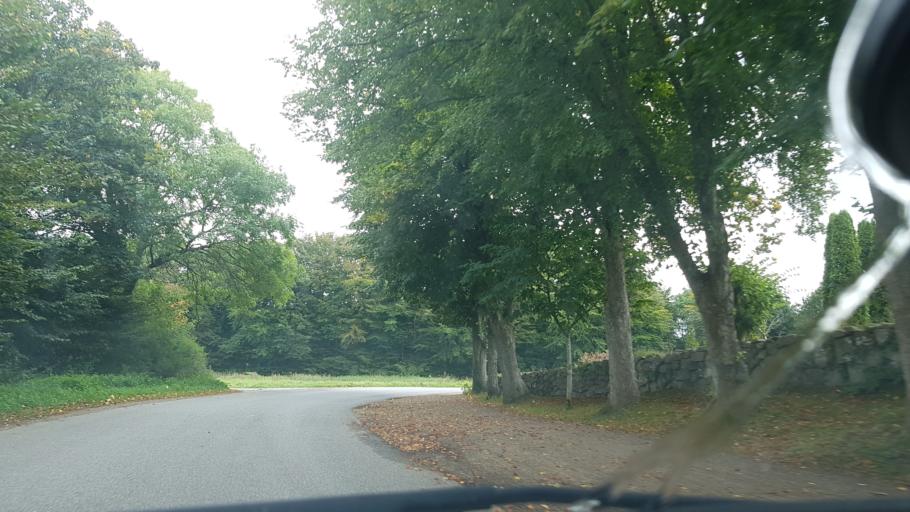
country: DK
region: South Denmark
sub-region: Vejle Kommune
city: Egtved
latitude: 55.5711
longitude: 9.2363
